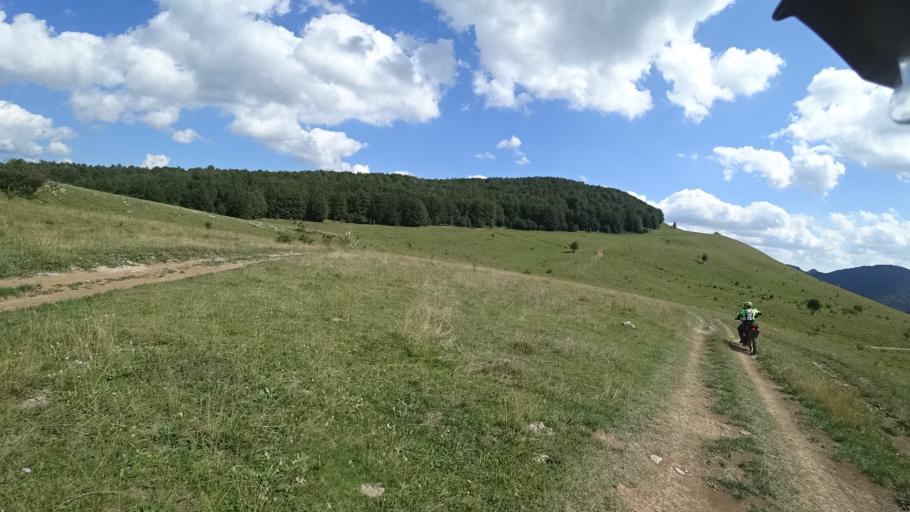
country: HR
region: Zadarska
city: Gracac
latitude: 44.4382
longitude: 15.9831
